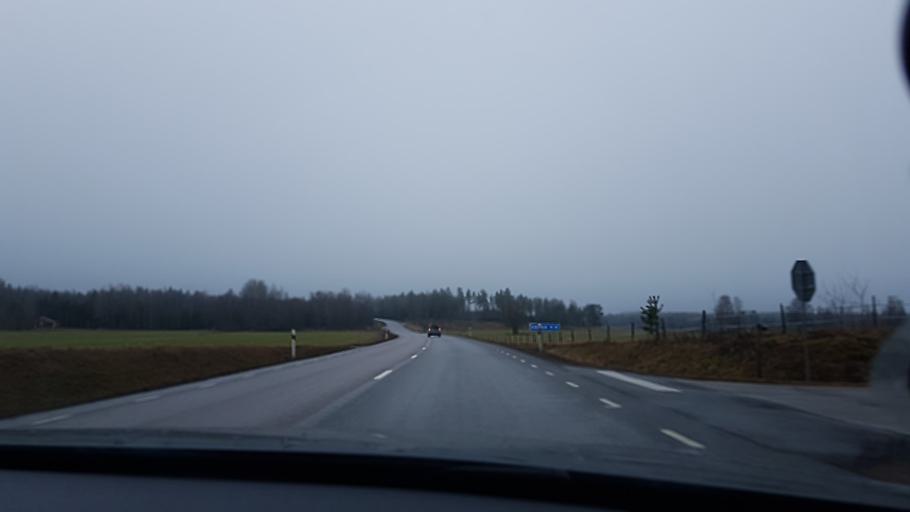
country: SE
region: Vaestra Goetaland
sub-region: Mariestads Kommun
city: Mariestad
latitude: 58.7927
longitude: 13.9668
